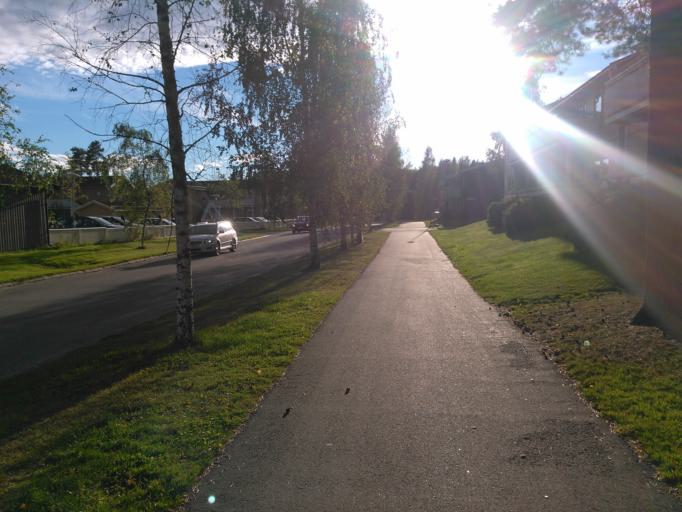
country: SE
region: Vaesterbotten
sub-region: Umea Kommun
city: Ersmark
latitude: 63.8079
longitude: 20.3390
